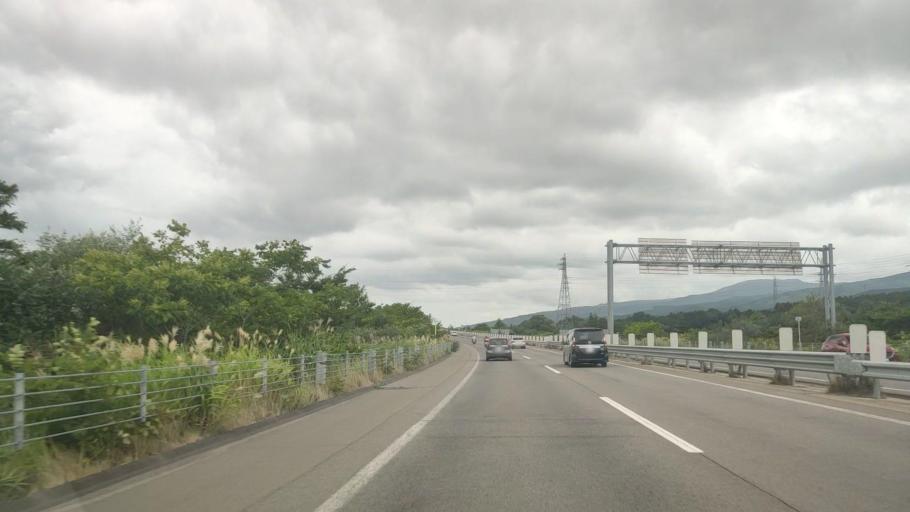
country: JP
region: Hokkaido
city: Nanae
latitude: 41.8562
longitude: 140.7373
